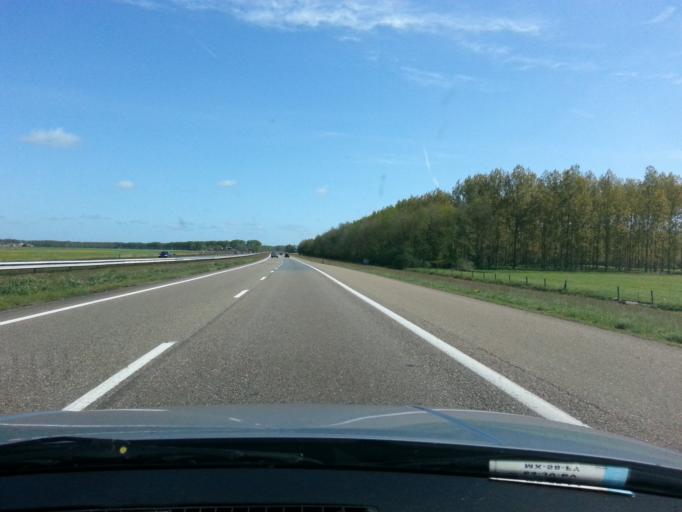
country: NL
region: Friesland
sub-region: Gemeente Opsterland
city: Tijnje
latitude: 52.9979
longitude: 5.9920
